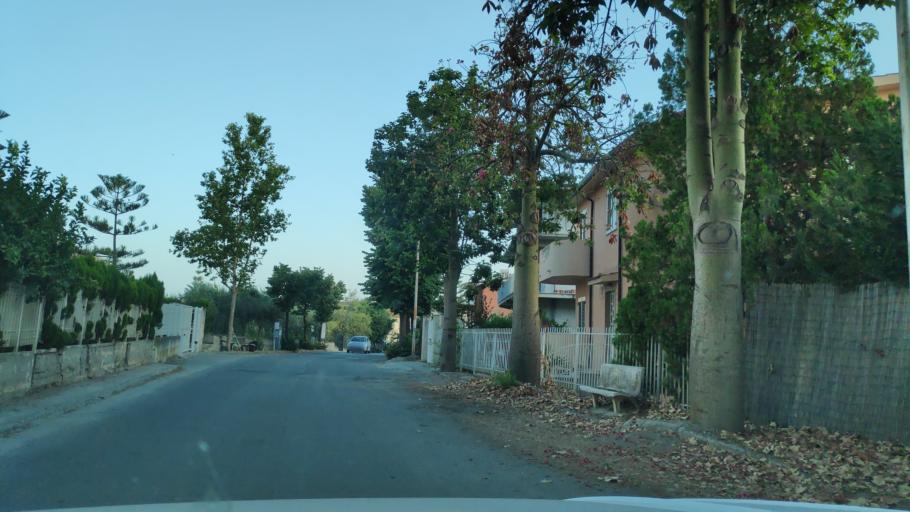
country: IT
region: Calabria
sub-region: Provincia di Reggio Calabria
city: Bova Marina
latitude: 37.9307
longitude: 15.9111
